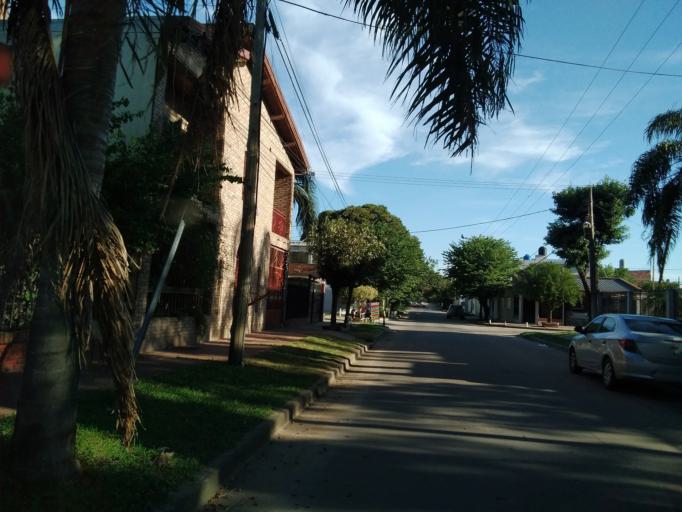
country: AR
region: Corrientes
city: Corrientes
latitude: -27.4731
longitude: -58.8098
